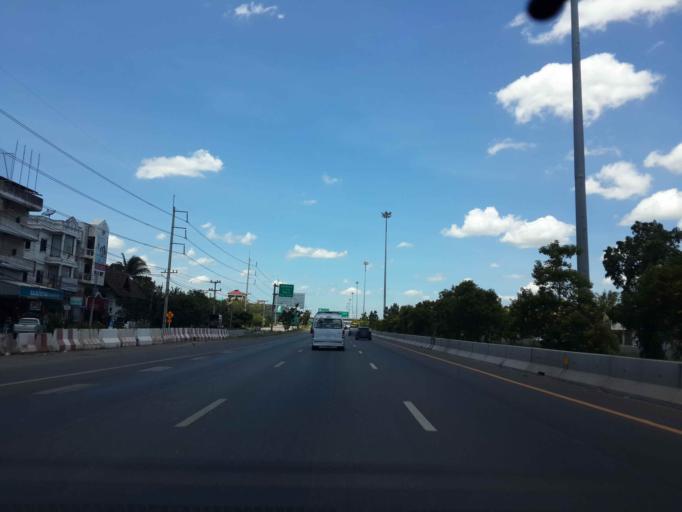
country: TH
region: Samut Songkhram
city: Samut Songkhram
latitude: 13.3943
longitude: 100.0017
